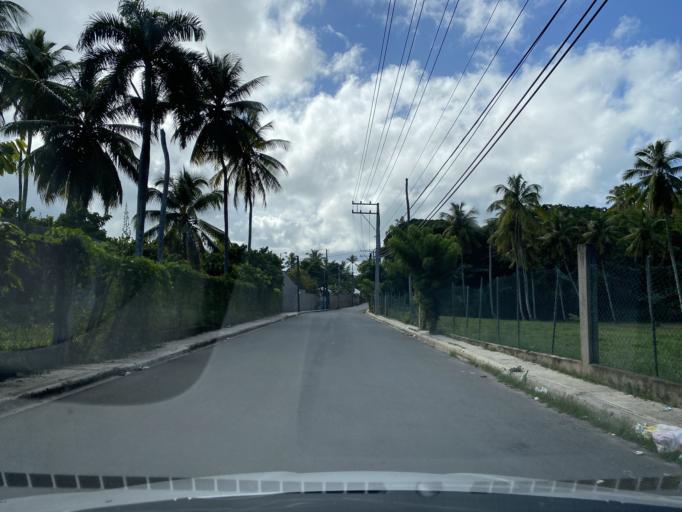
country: DO
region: Samana
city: Las Terrenas
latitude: 19.3109
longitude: -69.5478
